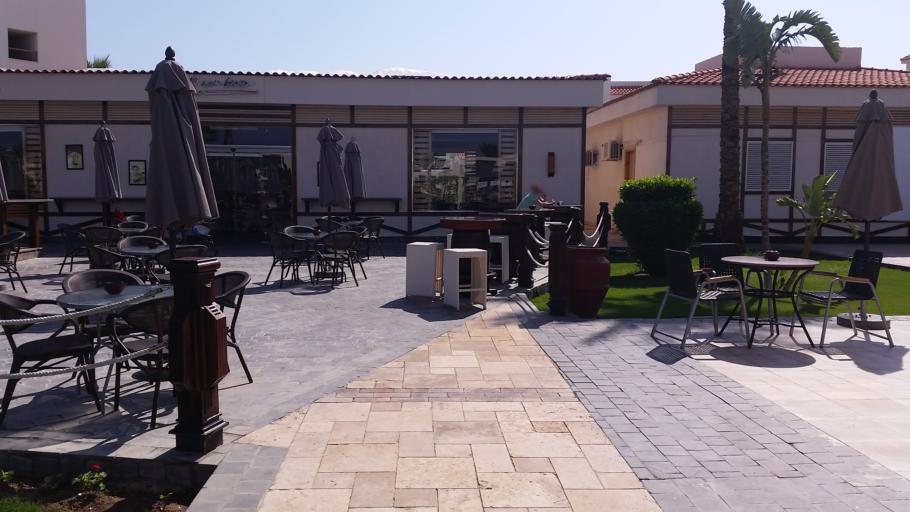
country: EG
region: Red Sea
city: Makadi Bay
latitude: 27.0971
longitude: 33.8326
